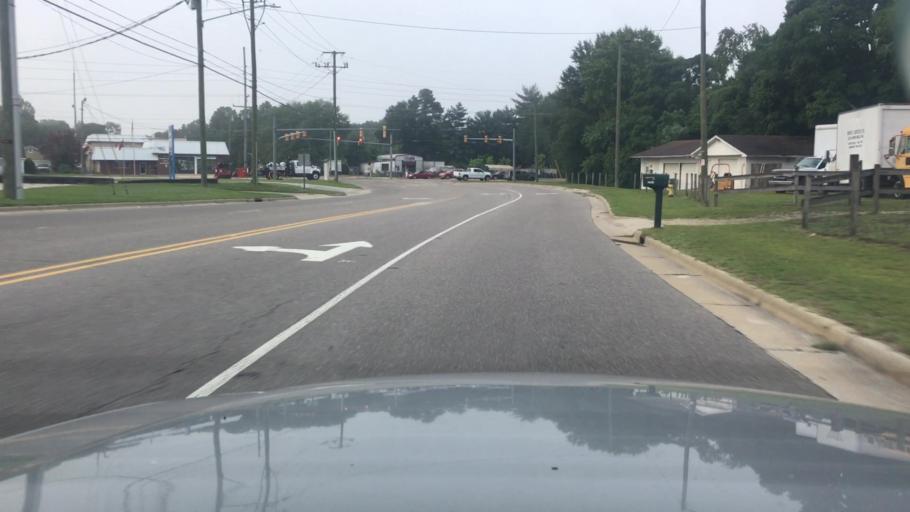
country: US
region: North Carolina
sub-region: Cumberland County
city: Hope Mills
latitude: 35.0154
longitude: -78.9354
